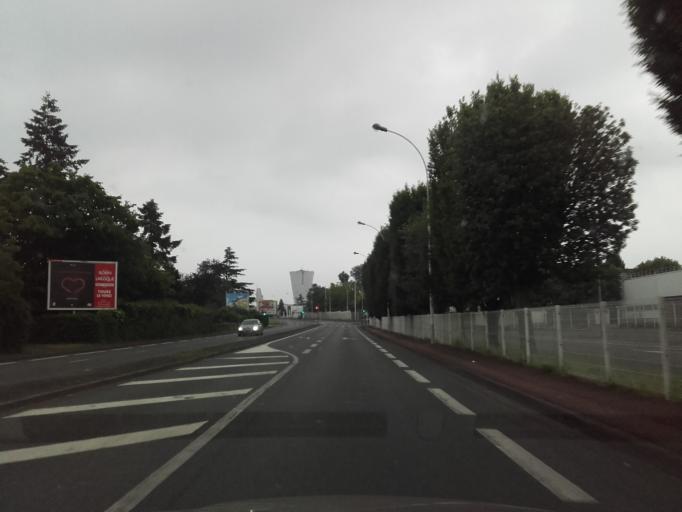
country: FR
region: Centre
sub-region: Departement d'Indre-et-Loire
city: Saint-Cyr-sur-Loire
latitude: 47.4295
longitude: 0.6970
